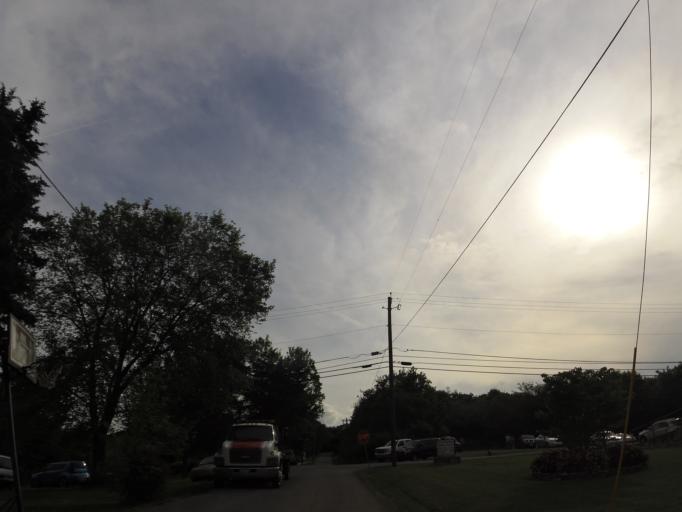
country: US
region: Tennessee
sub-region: Knox County
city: Mascot
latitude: 36.0398
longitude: -83.8197
